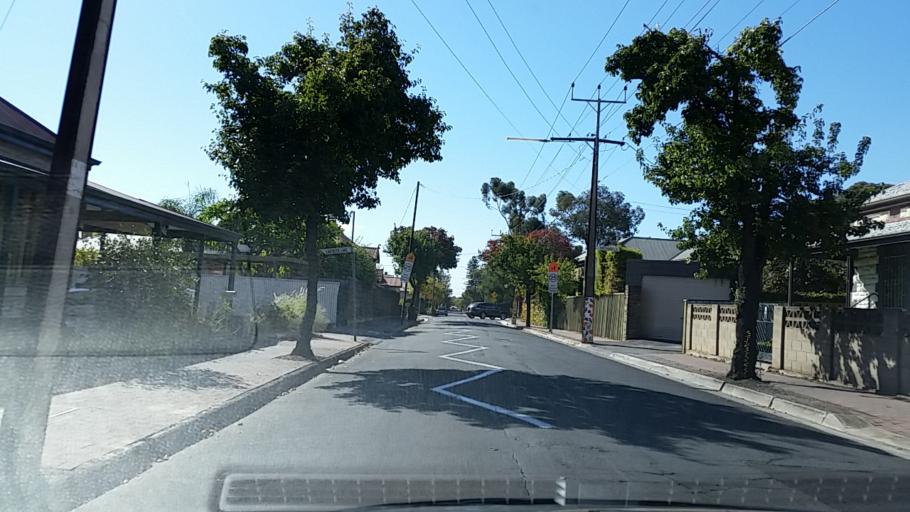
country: AU
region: South Australia
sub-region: Prospect
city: Prospect
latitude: -34.8864
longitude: 138.5894
